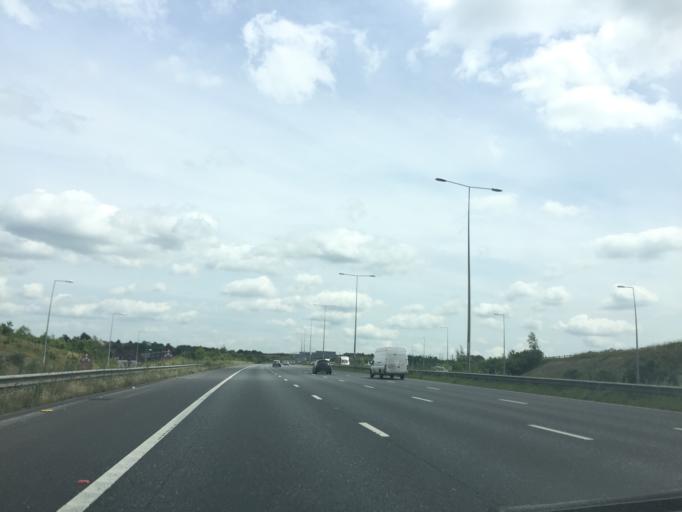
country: GB
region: England
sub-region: Kent
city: Gravesend
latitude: 51.4172
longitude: 0.3548
